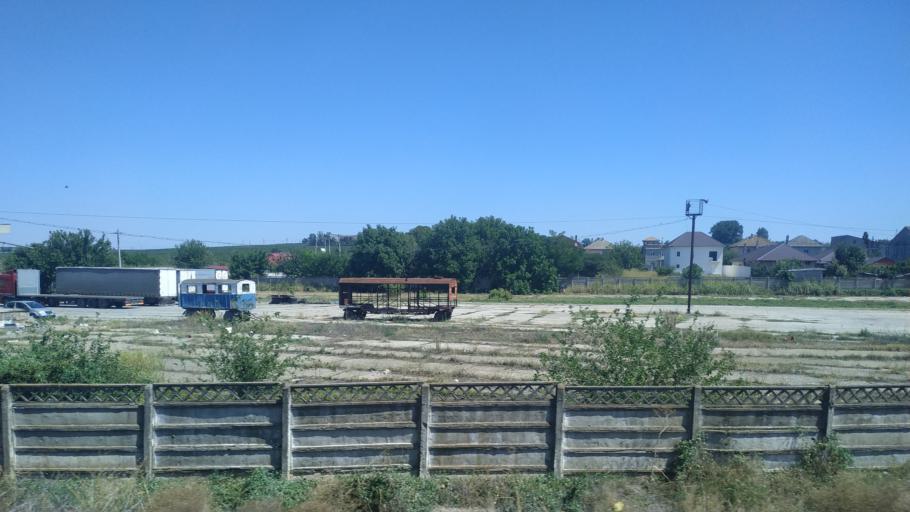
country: RO
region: Constanta
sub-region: Oras Murfatlar
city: Murfatlar
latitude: 44.1798
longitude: 28.3995
